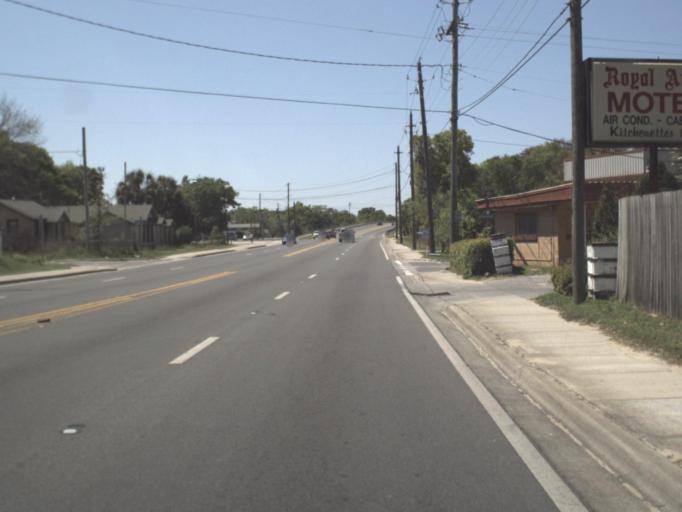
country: US
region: Florida
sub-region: Escambia County
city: West Pensacola
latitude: 30.4241
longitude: -87.2621
